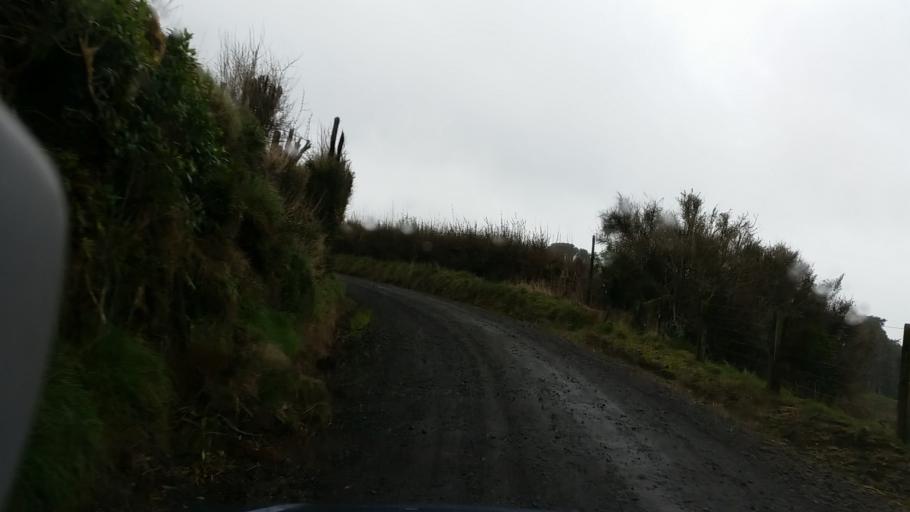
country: NZ
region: Taranaki
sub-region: South Taranaki District
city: Eltham
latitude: -39.2812
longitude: 174.3350
